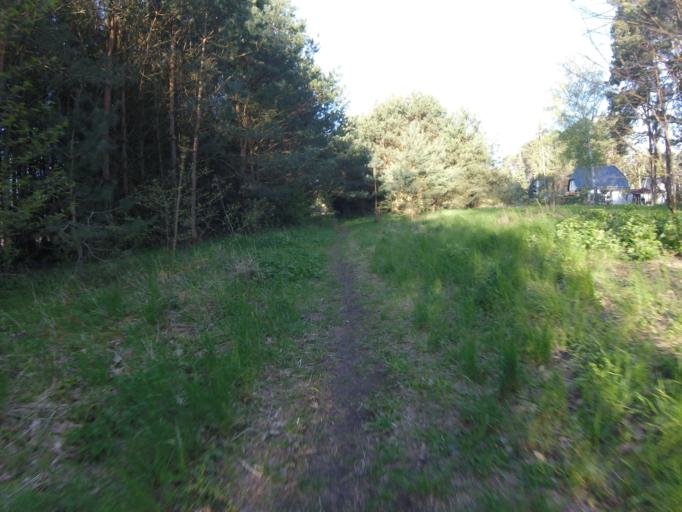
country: DE
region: Brandenburg
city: Bestensee
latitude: 52.2888
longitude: 13.7071
